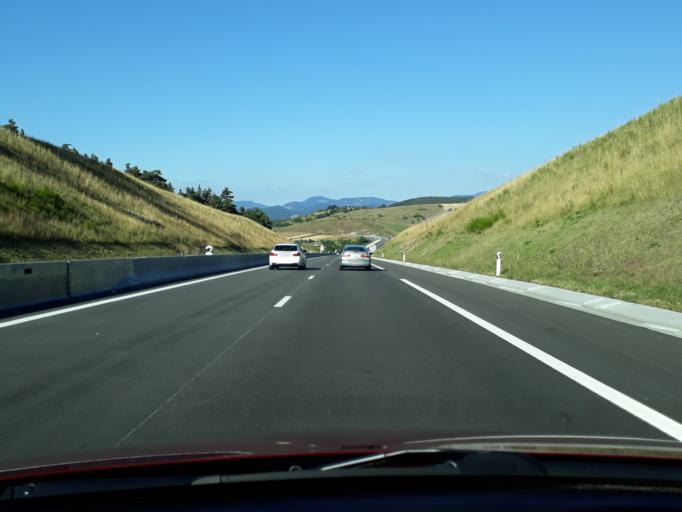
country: FR
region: Auvergne
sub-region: Departement de la Haute-Loire
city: Vals-pres-le-Puy
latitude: 45.0128
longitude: 3.8870
